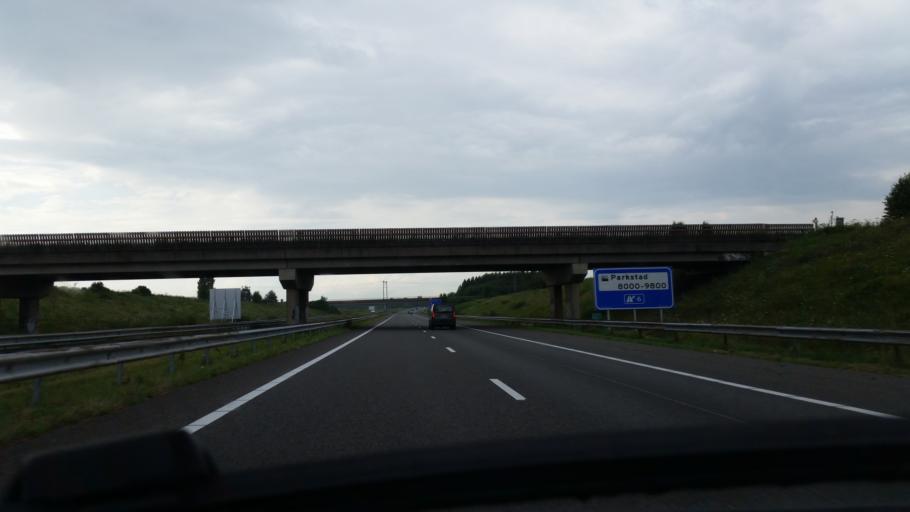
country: NL
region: Limburg
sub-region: Gemeente Voerendaal
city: Voerendaal
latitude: 50.8878
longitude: 5.9429
